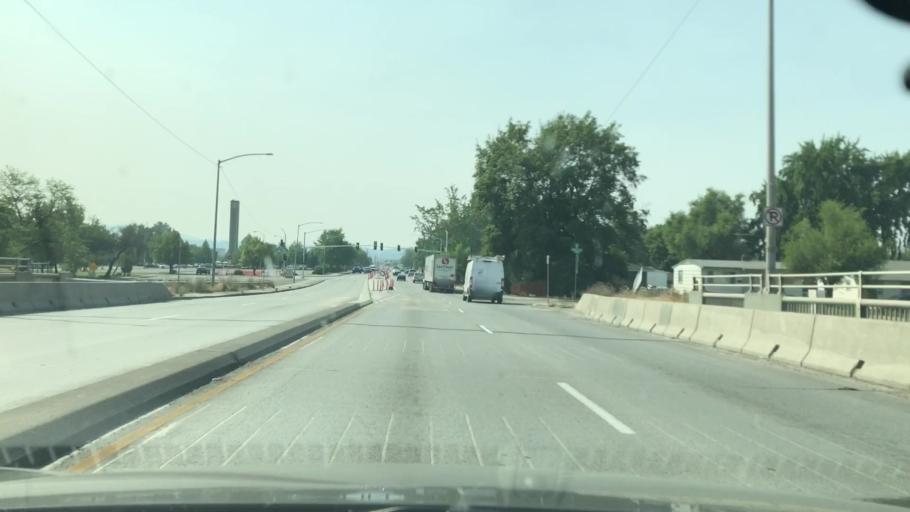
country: US
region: Washington
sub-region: Spokane County
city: Spokane
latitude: 47.6780
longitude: -117.3637
